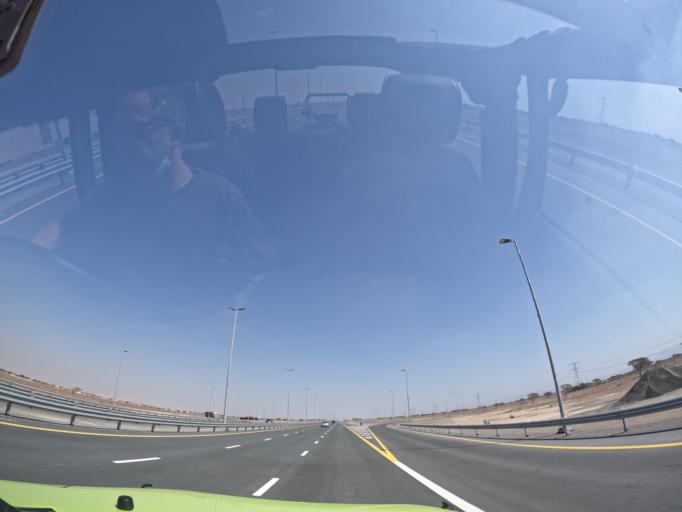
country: AE
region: Ash Shariqah
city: Adh Dhayd
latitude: 24.9529
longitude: 55.8361
